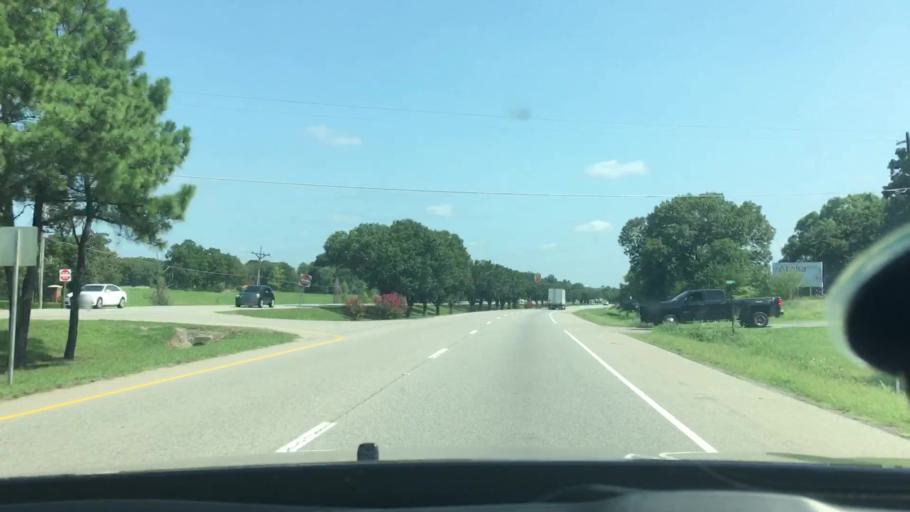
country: US
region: Oklahoma
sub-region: Atoka County
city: Atoka
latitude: 34.3563
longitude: -96.1468
